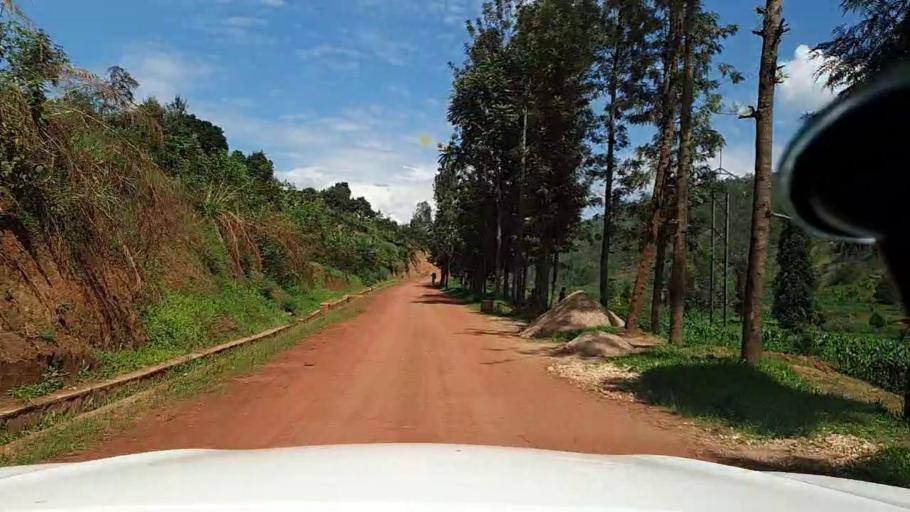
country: RW
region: Kigali
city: Kigali
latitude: -1.7905
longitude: 29.8840
